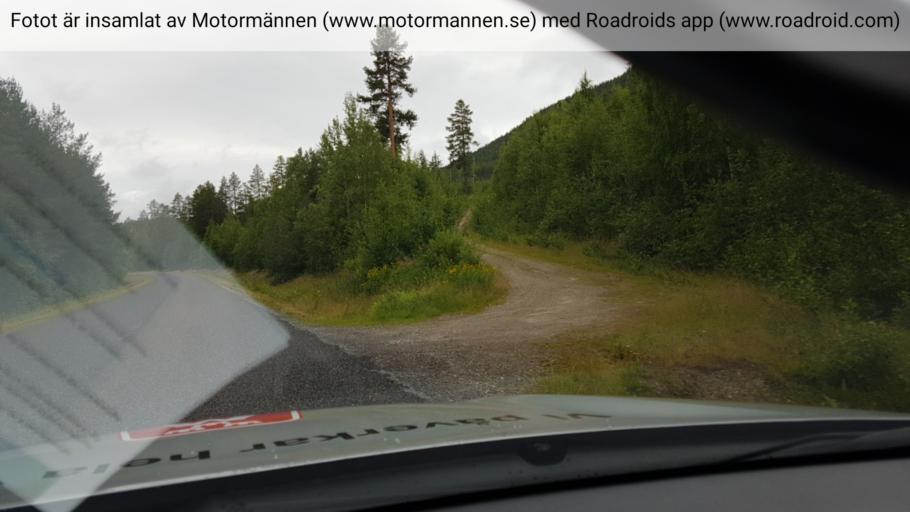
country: SE
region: Norrbotten
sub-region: Gallivare Kommun
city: Gaellivare
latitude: 66.4978
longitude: 20.5887
